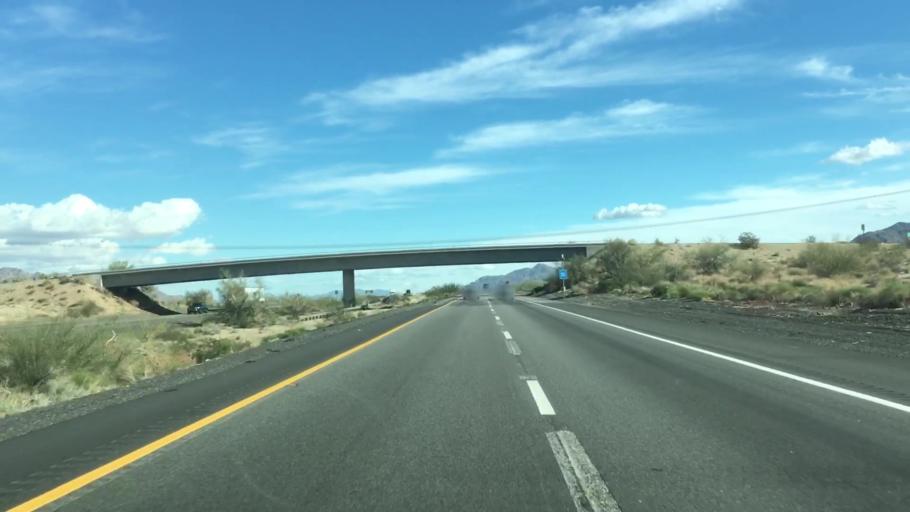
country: US
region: California
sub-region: Riverside County
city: Mecca
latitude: 33.6680
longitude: -115.6556
